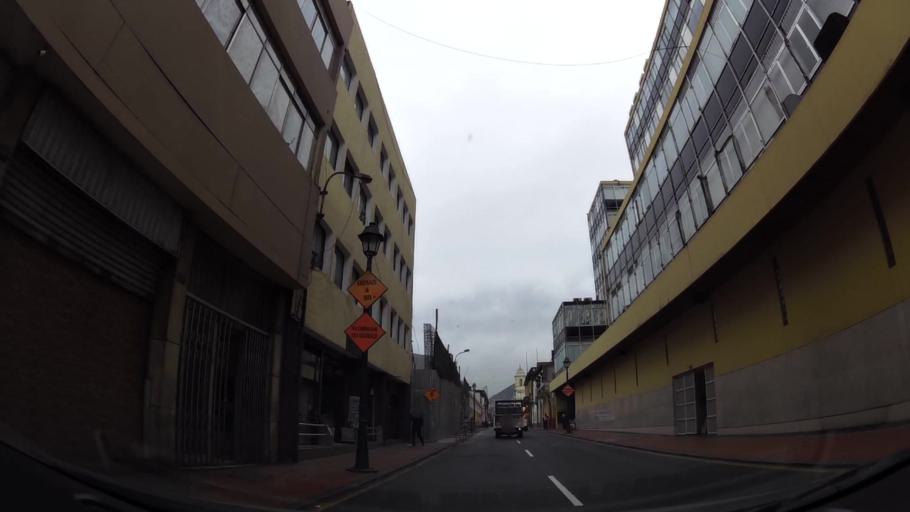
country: PE
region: Lima
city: Lima
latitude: -12.0463
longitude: -77.0287
